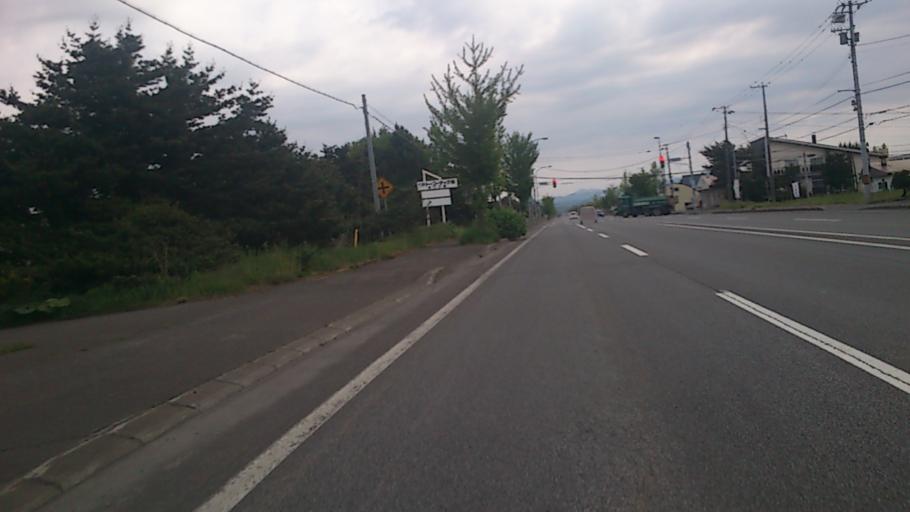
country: JP
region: Hokkaido
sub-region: Asahikawa-shi
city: Asahikawa
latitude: 43.8346
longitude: 142.4723
